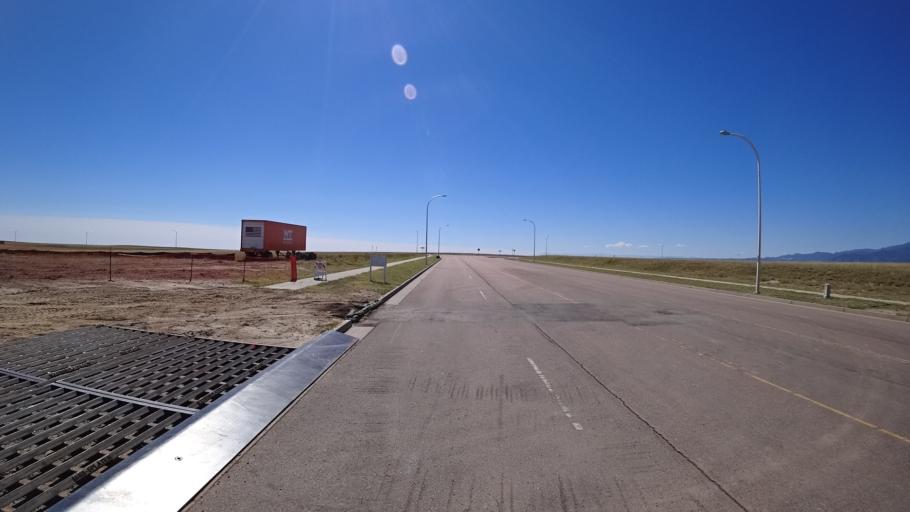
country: US
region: Colorado
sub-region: El Paso County
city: Security-Widefield
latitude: 38.7772
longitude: -104.6998
